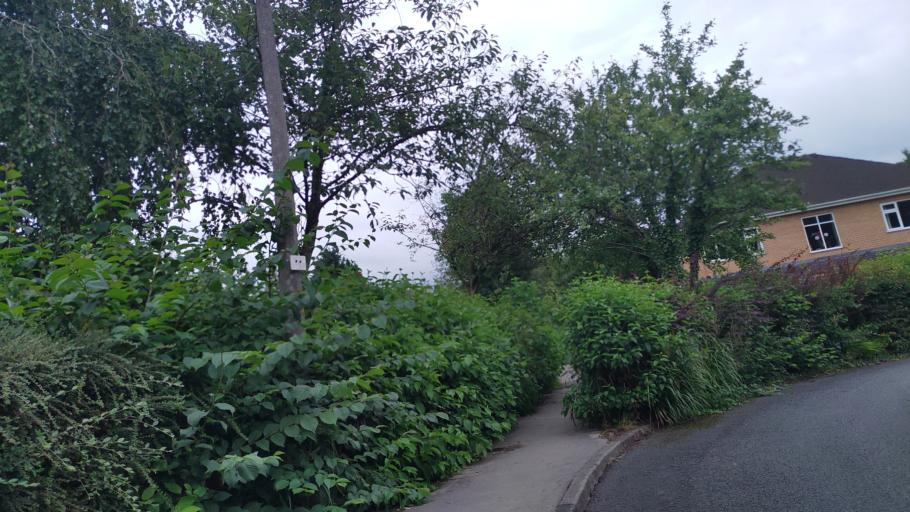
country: GB
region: England
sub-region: Lancashire
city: Euxton
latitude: 53.6593
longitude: -2.6503
